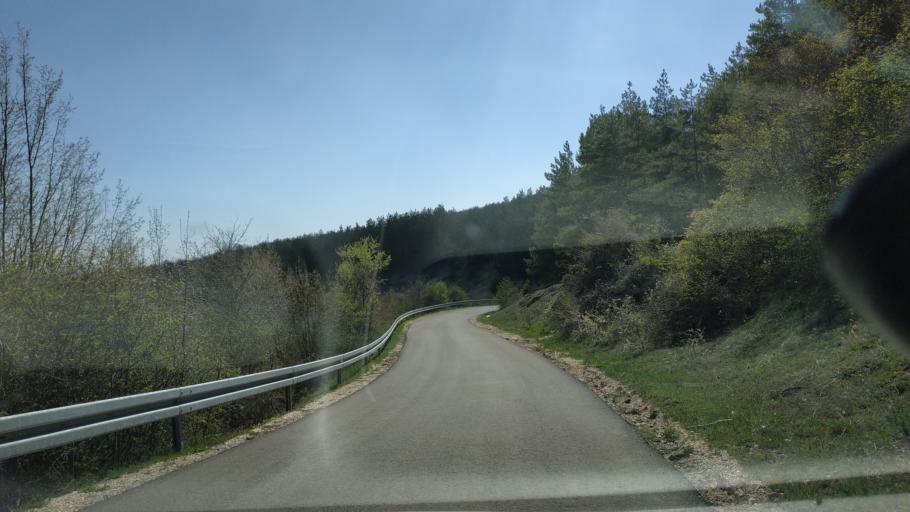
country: RS
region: Central Serbia
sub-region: Zajecarski Okrug
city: Soko Banja
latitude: 43.5784
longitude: 21.8951
